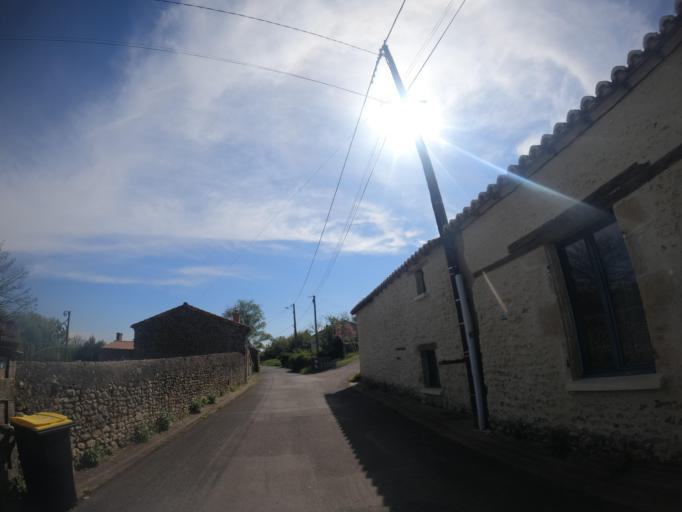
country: FR
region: Poitou-Charentes
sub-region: Departement des Deux-Sevres
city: Saint-Varent
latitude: 46.9105
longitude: -0.2137
